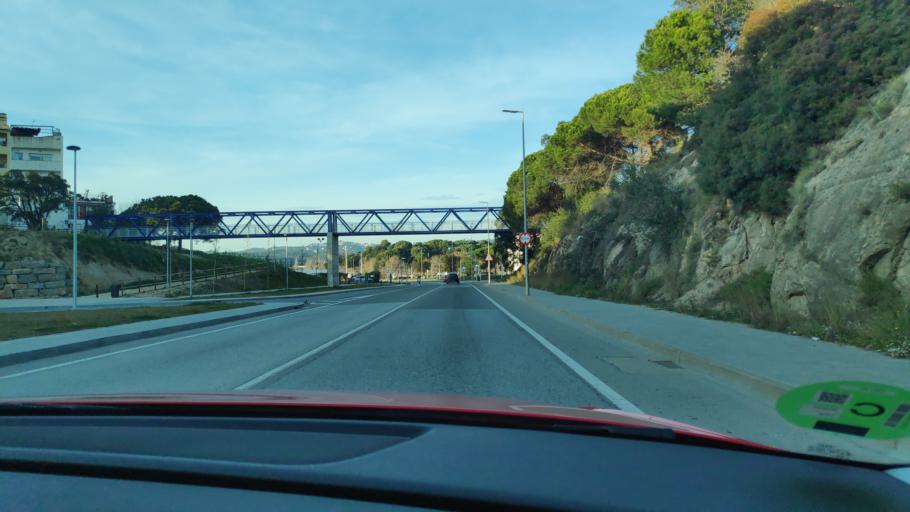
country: ES
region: Catalonia
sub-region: Provincia de Girona
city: Lloret de Mar
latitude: 41.7056
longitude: 2.8353
